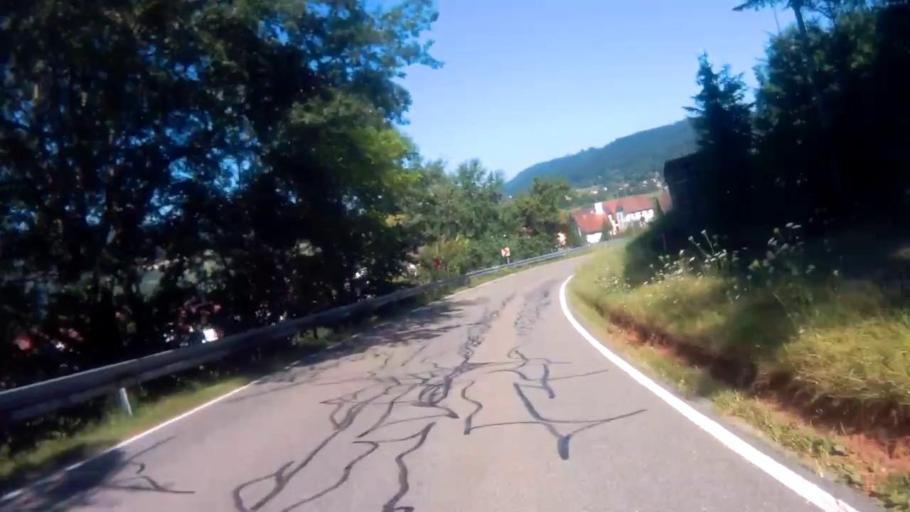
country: DE
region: Baden-Wuerttemberg
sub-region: Freiburg Region
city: Hausen
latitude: 47.6794
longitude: 7.8109
